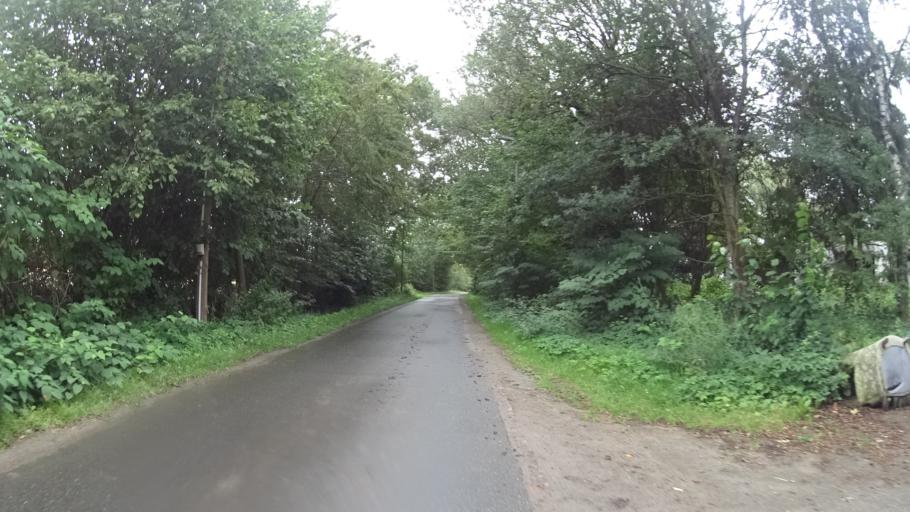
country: DE
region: Schleswig-Holstein
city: Lasbek
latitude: 53.7322
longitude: 10.3751
